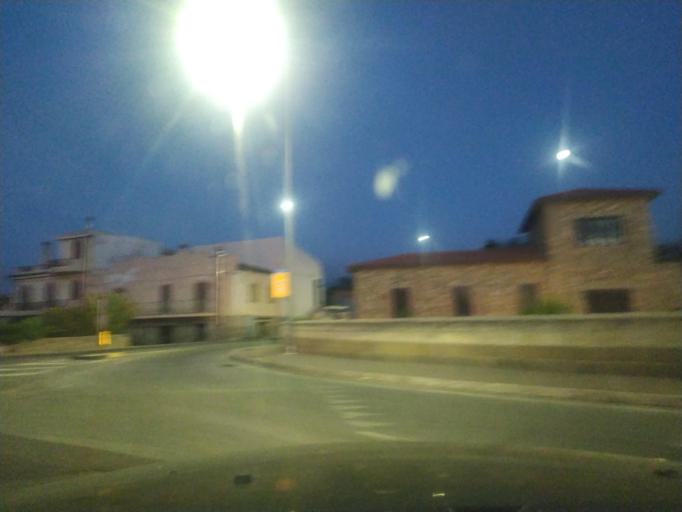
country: IT
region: Sicily
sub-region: Messina
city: Terme
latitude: 38.1455
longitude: 15.1583
